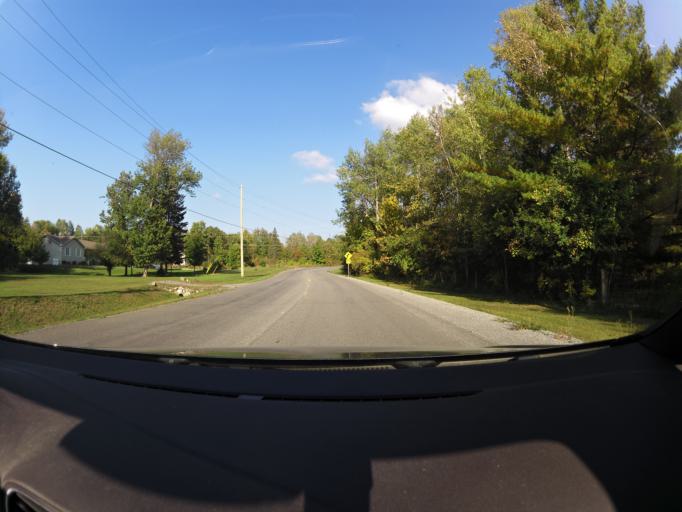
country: CA
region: Ontario
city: Arnprior
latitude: 45.4427
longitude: -76.2567
